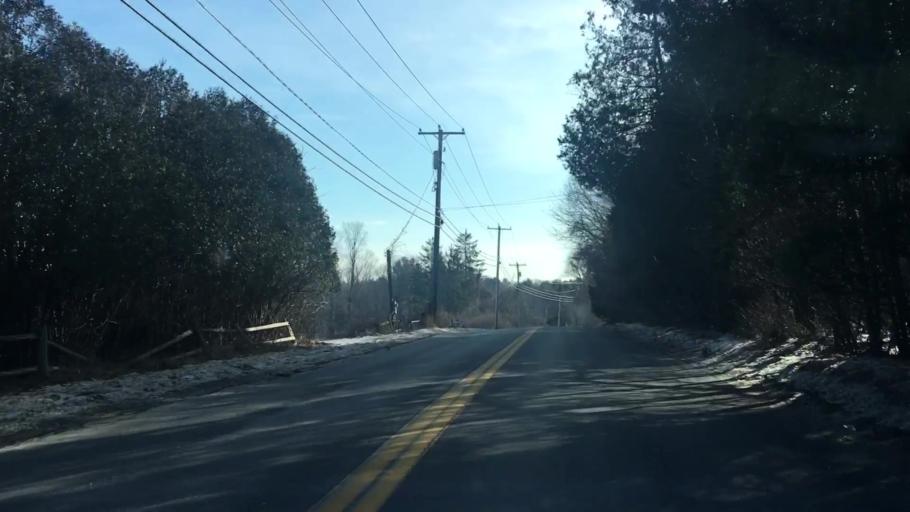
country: US
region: Maine
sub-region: Androscoggin County
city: Auburn
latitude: 44.1247
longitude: -70.2618
